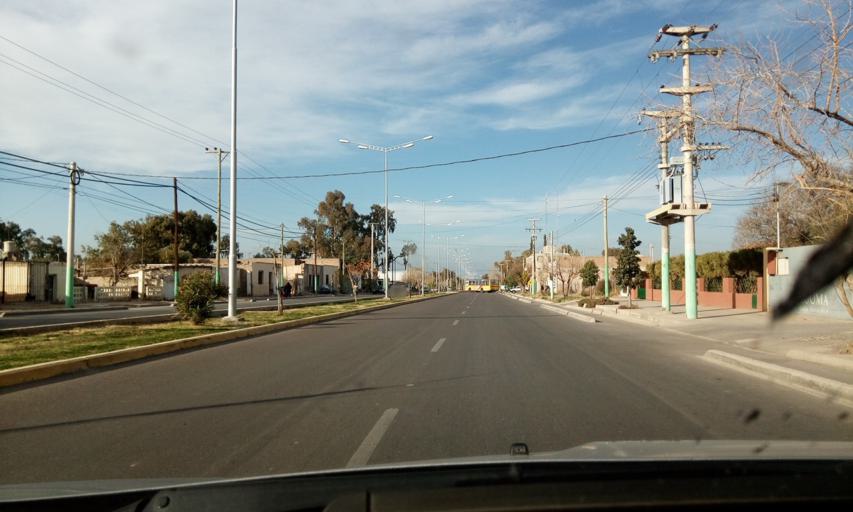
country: AR
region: San Juan
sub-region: Departamento de Rivadavia
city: Rivadavia
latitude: -31.5246
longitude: -68.6259
